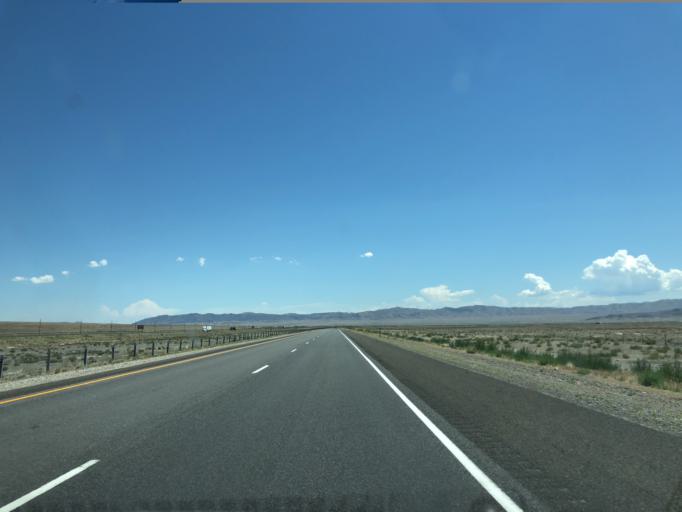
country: US
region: Utah
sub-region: Tooele County
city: Grantsville
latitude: 40.7254
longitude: -113.1732
